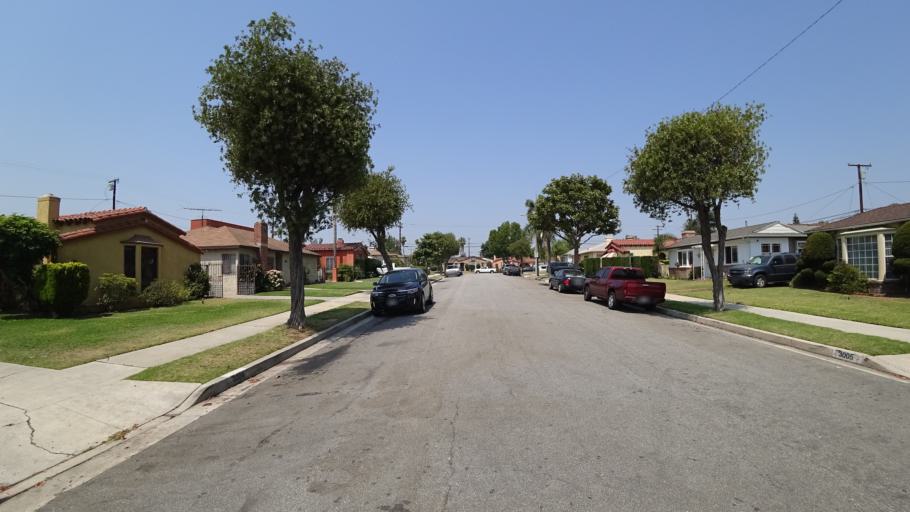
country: US
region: California
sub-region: Los Angeles County
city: Inglewood
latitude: 33.9657
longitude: -118.3256
